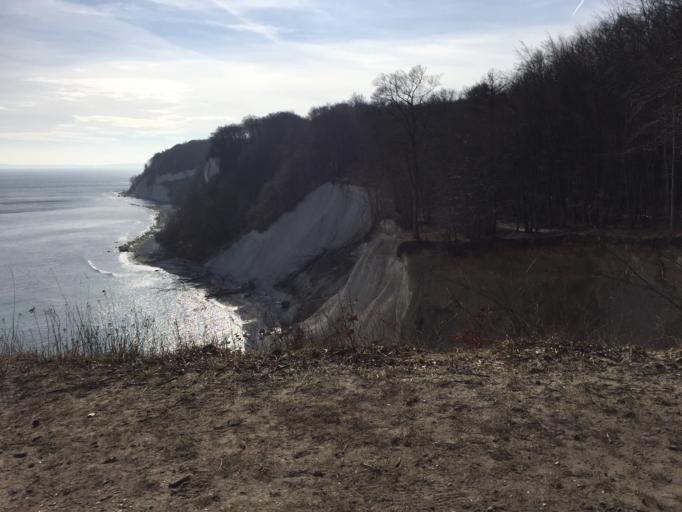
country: DE
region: Mecklenburg-Vorpommern
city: Sassnitz
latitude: 54.5286
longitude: 13.6741
